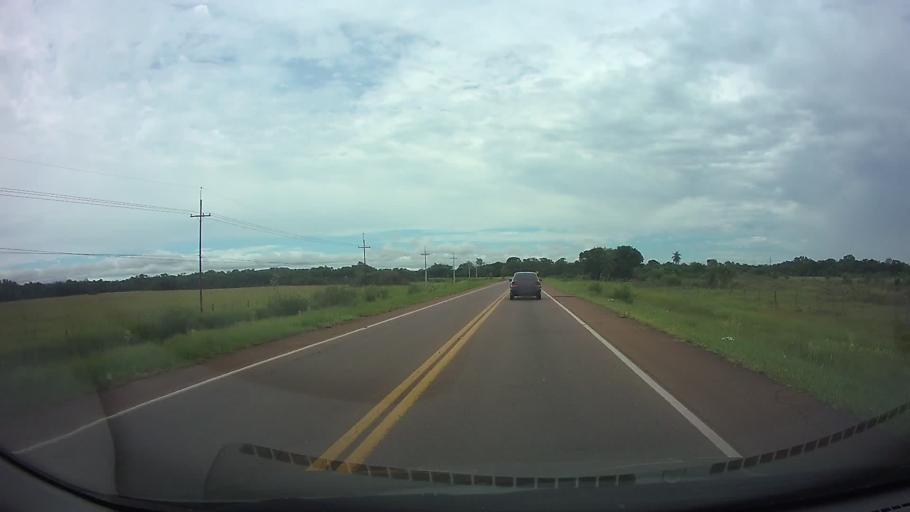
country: PY
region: Paraguari
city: Carapegua
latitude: -25.7214
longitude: -57.2017
